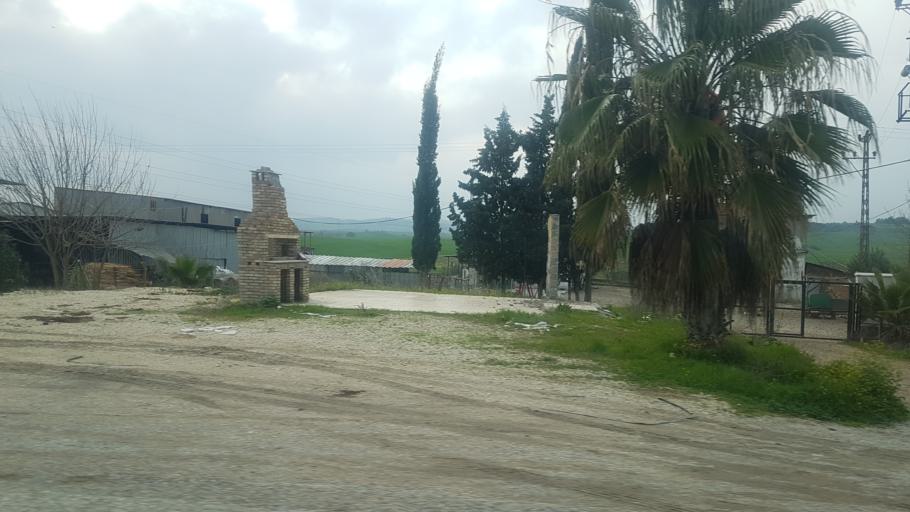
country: TR
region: Mersin
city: Yenice
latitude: 37.0668
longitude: 35.1718
